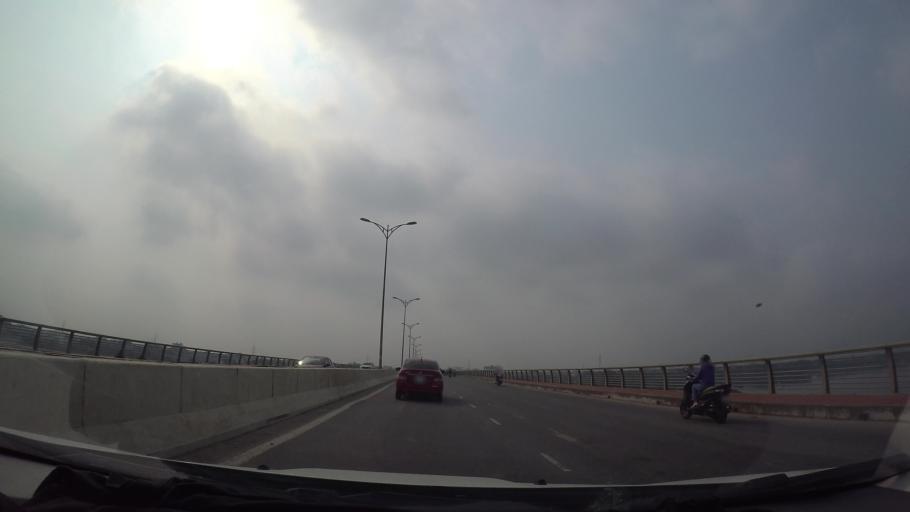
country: VN
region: Da Nang
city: Cam Le
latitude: 16.0156
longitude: 108.2138
